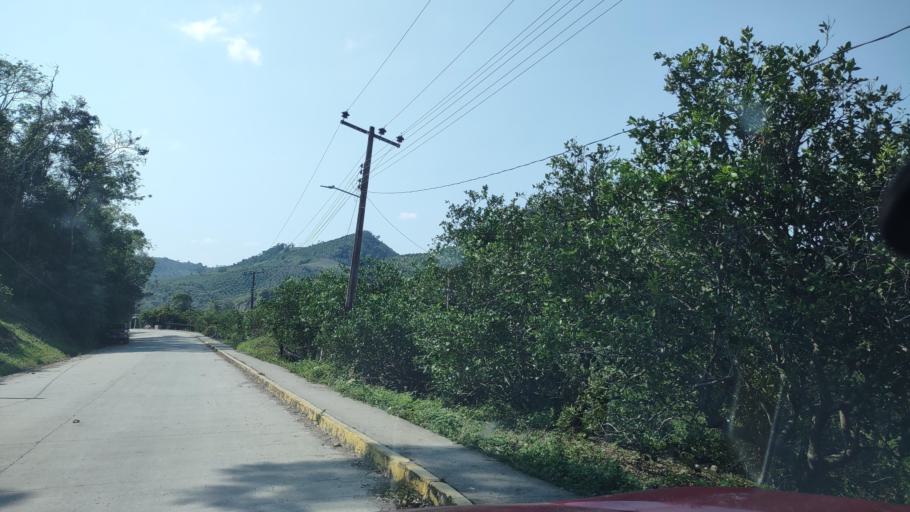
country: MX
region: Veracruz
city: Agua Dulce
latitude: 20.3144
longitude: -97.1744
